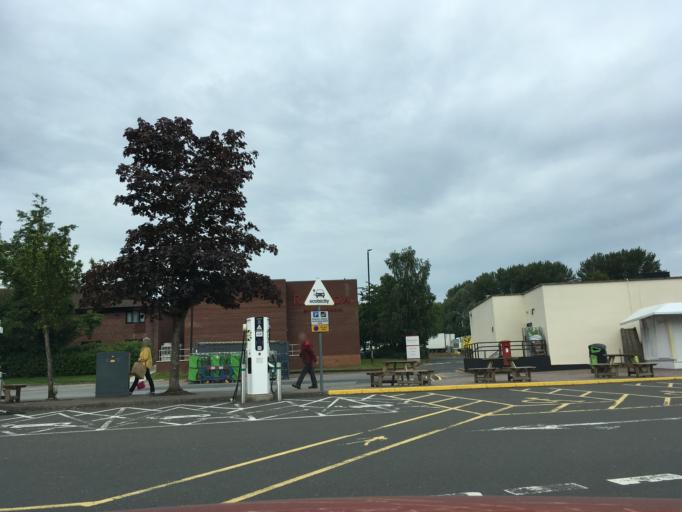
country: GB
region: England
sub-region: North Somerset
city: Easton-in-Gordano
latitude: 51.4775
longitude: -2.7067
